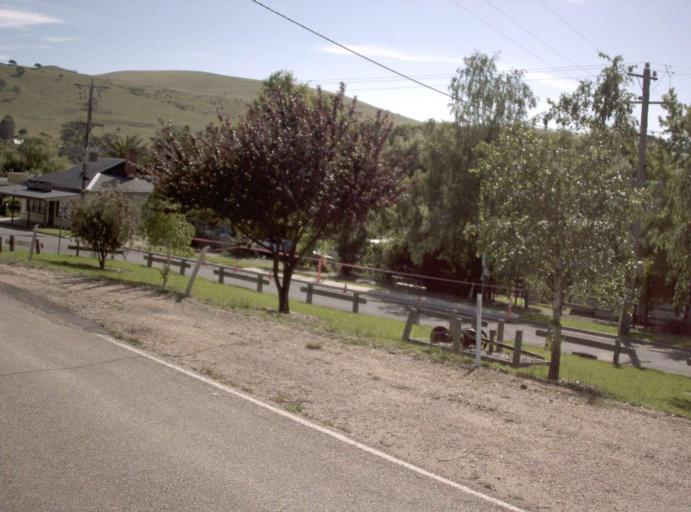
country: AU
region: Victoria
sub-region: East Gippsland
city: Lakes Entrance
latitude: -37.4999
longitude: 148.1717
